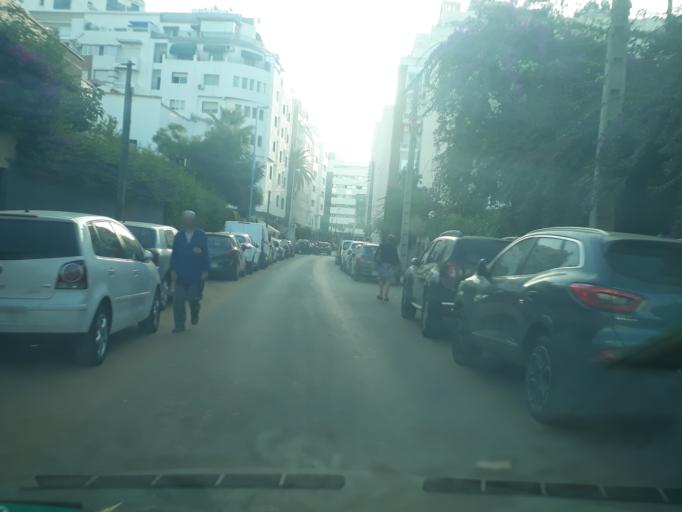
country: MA
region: Grand Casablanca
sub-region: Casablanca
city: Casablanca
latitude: 33.5795
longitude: -7.6272
